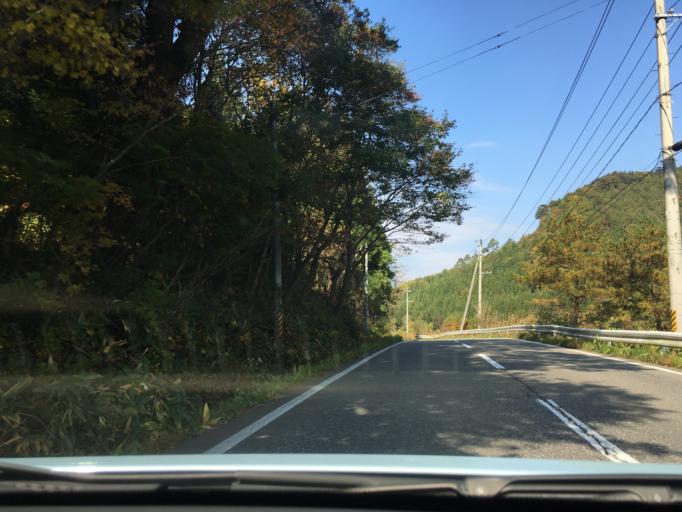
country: JP
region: Fukushima
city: Inawashiro
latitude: 37.4213
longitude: 140.0357
